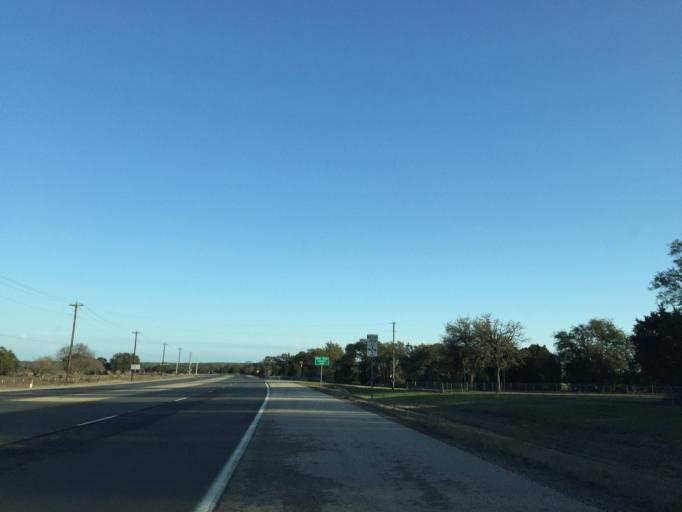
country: US
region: Texas
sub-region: Williamson County
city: Florence
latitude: 30.7382
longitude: -97.7997
